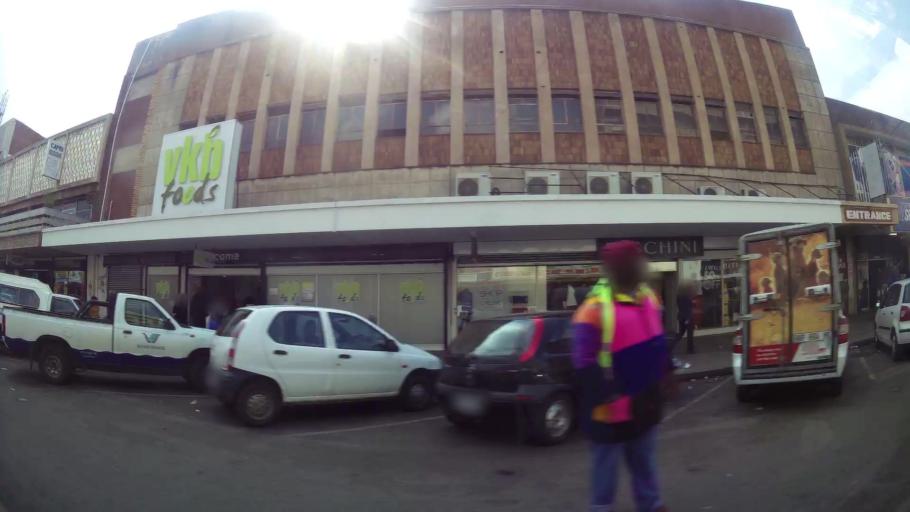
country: ZA
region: Gauteng
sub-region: Sedibeng District Municipality
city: Vereeniging
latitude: -26.6734
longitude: 27.9306
